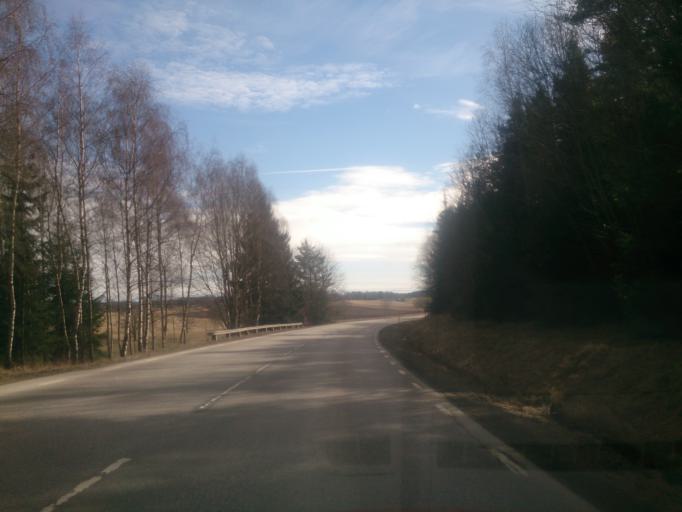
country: SE
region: OEstergoetland
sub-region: Finspangs Kommun
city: Finspang
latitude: 58.6548
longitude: 15.8090
